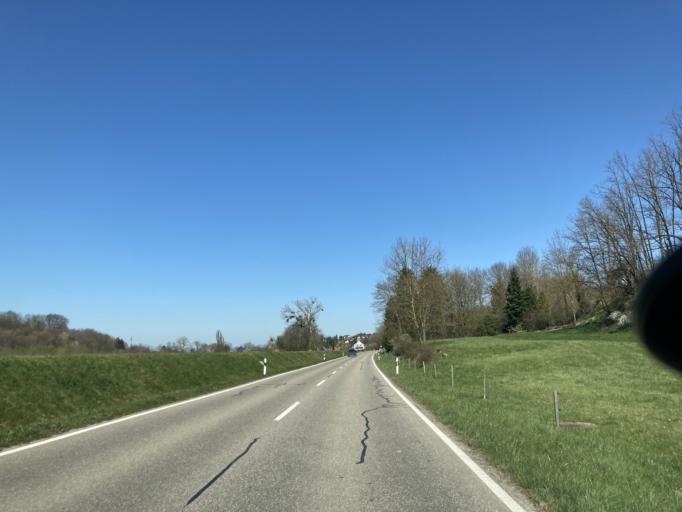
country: DE
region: Baden-Wuerttemberg
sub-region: Freiburg Region
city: Schliengen
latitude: 47.7464
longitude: 7.5913
